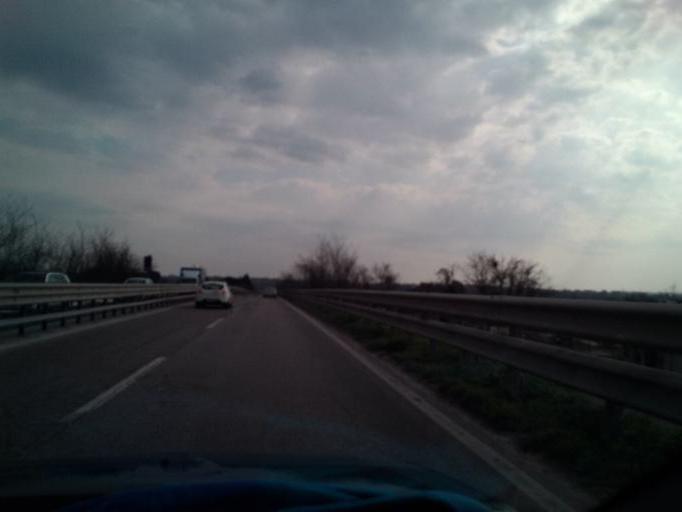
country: IT
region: Veneto
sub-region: Provincia di Verona
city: Pescantina
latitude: 45.4936
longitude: 10.8581
